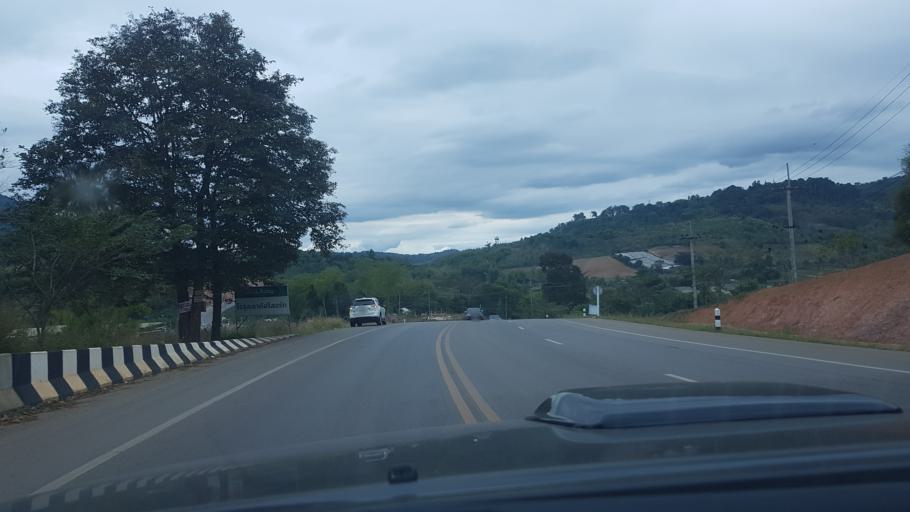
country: TH
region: Phetchabun
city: Khao Kho
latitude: 16.5705
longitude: 101.0036
